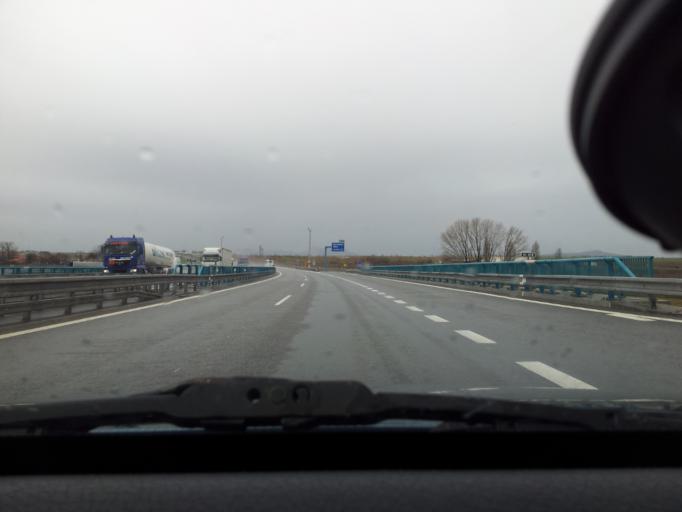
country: SK
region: Nitriansky
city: Zlate Moravce
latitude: 48.3510
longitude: 18.3767
